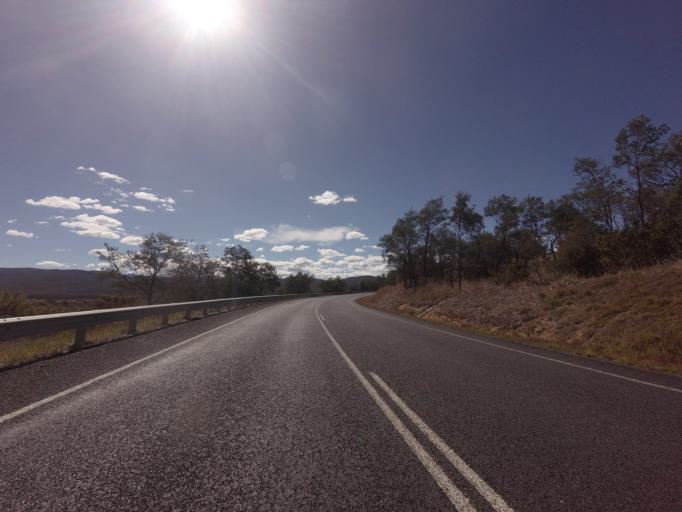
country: AU
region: Tasmania
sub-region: Break O'Day
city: St Helens
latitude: -41.7249
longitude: 147.8256
